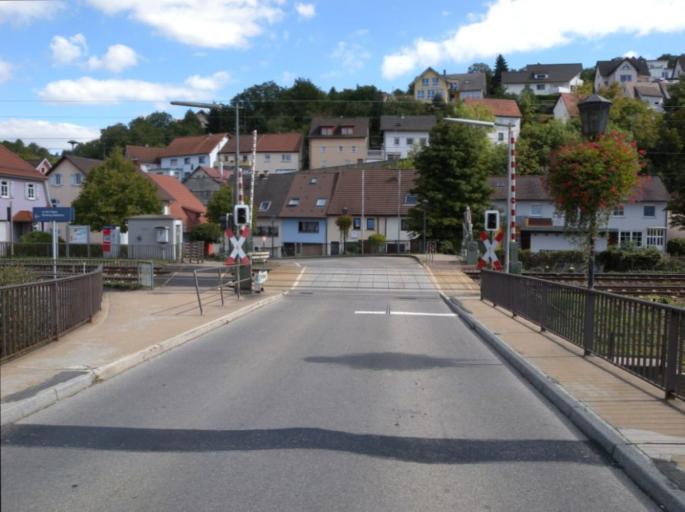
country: DE
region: Baden-Wuerttemberg
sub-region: Regierungsbezirk Stuttgart
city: Neudenau
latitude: 49.2810
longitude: 9.2595
